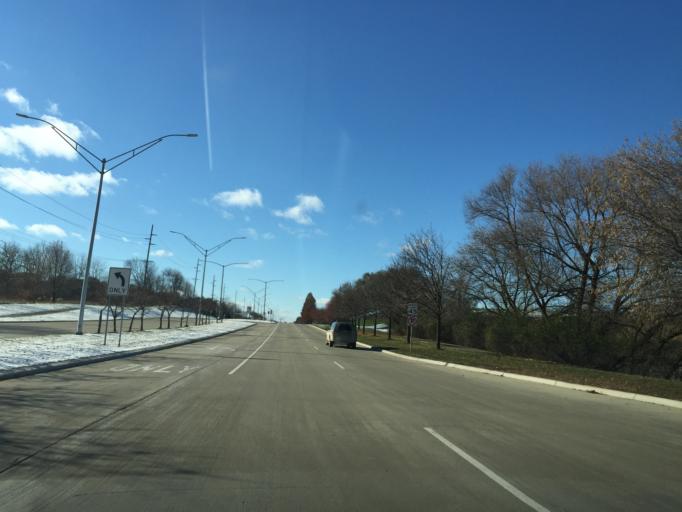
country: US
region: Michigan
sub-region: Oakland County
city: Auburn Hills
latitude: 42.6499
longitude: -83.2243
